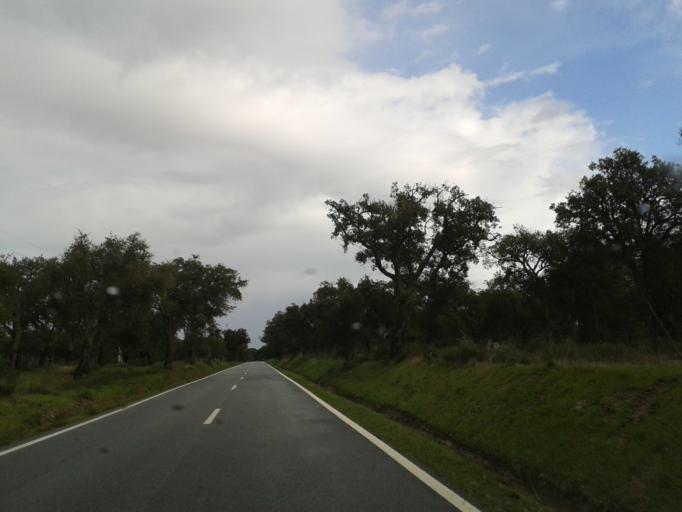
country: PT
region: Santarem
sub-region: Benavente
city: Poceirao
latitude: 38.8193
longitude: -8.7753
